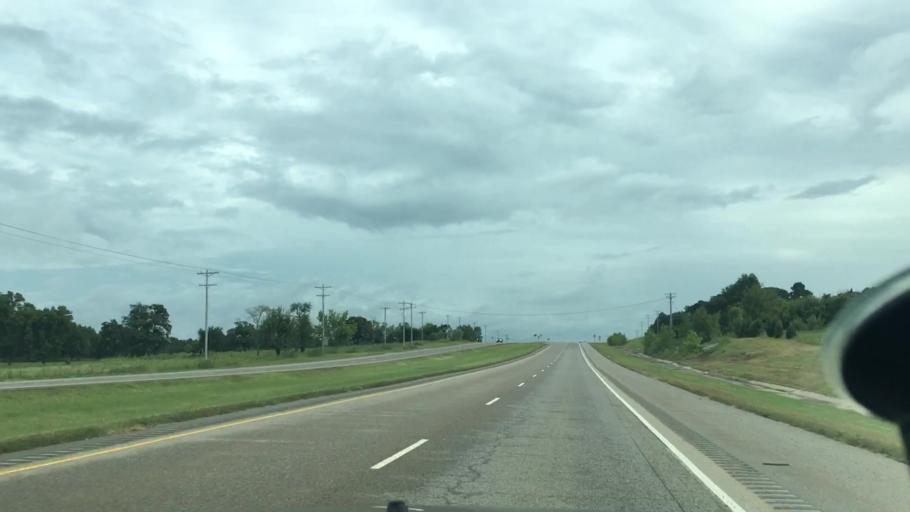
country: US
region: Oklahoma
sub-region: Seminole County
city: Seminole
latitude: 35.3372
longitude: -96.6717
